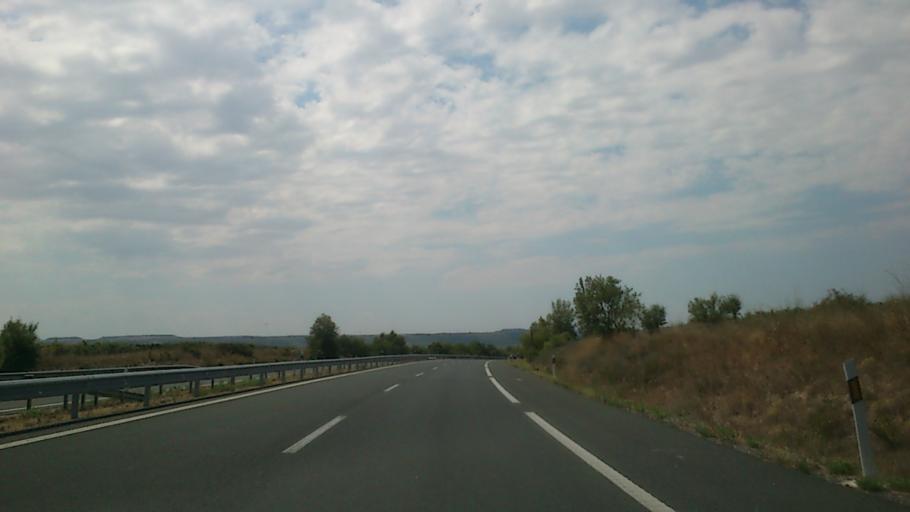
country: ES
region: La Rioja
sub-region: Provincia de La Rioja
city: Torremontalbo
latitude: 42.4780
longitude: -2.6725
